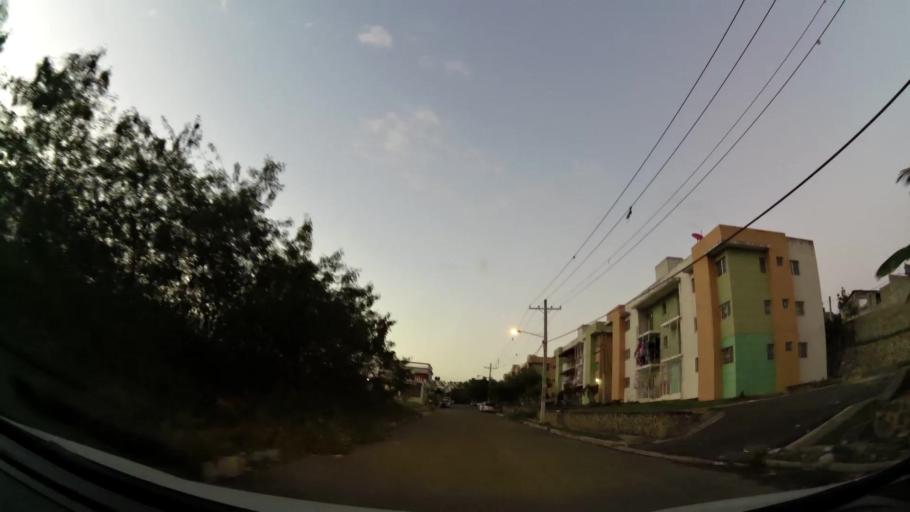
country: DO
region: Nacional
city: La Agustina
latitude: 18.5446
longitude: -69.9438
